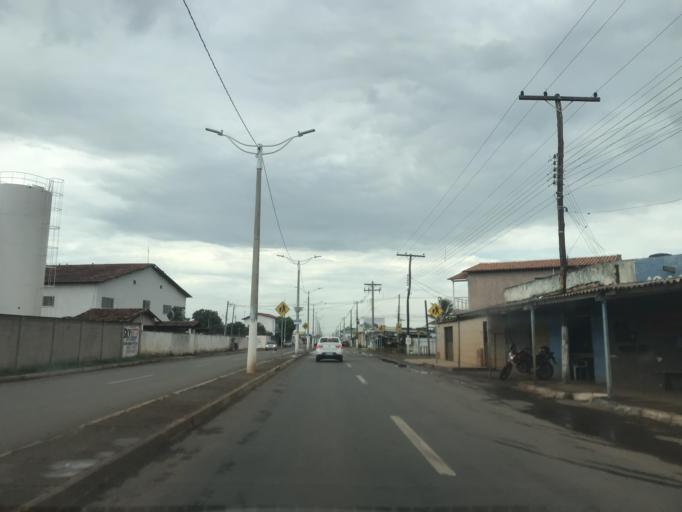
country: BR
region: Goias
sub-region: Luziania
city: Luziania
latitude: -16.2012
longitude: -47.9226
